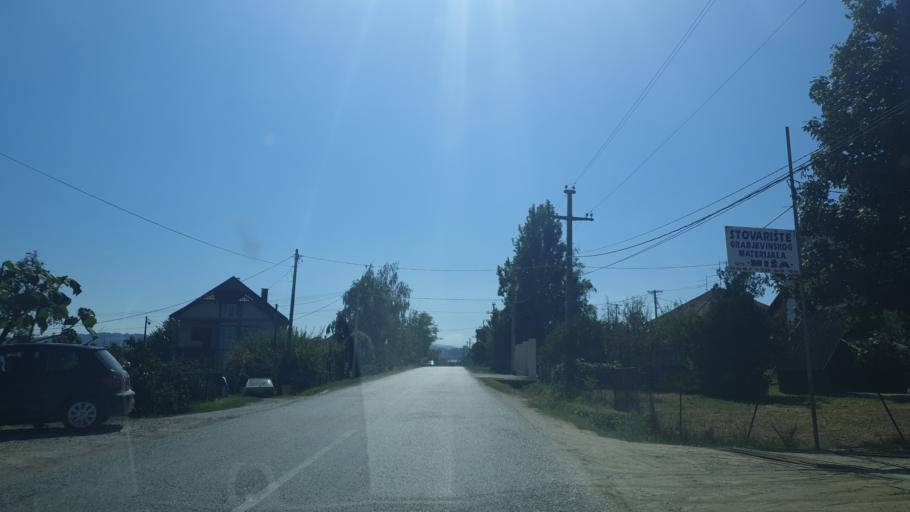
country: RS
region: Central Serbia
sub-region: Kolubarski Okrug
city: Mionica
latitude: 44.2428
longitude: 20.0809
